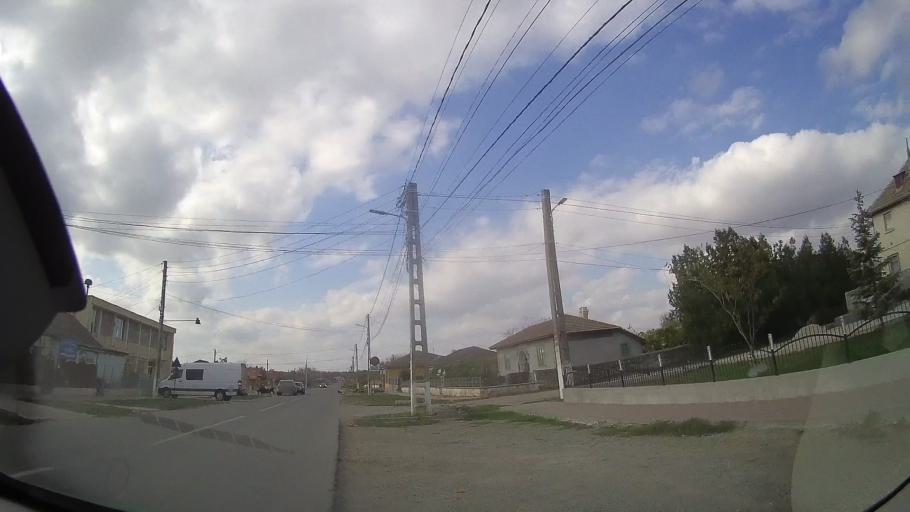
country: RO
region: Constanta
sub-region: Comuna Pecineaga
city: Pecineaga
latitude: 43.8953
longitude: 28.4970
